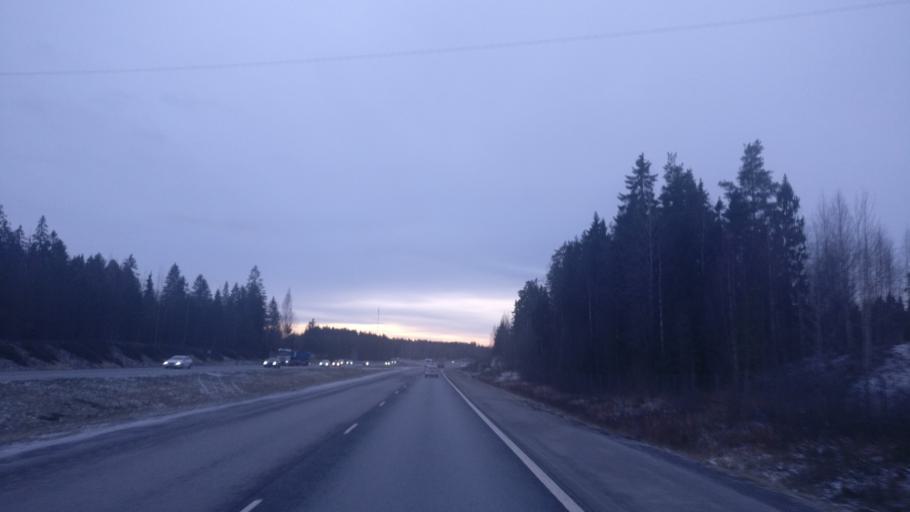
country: FI
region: Uusimaa
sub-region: Helsinki
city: Jaervenpaeae
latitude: 60.5556
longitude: 25.1870
